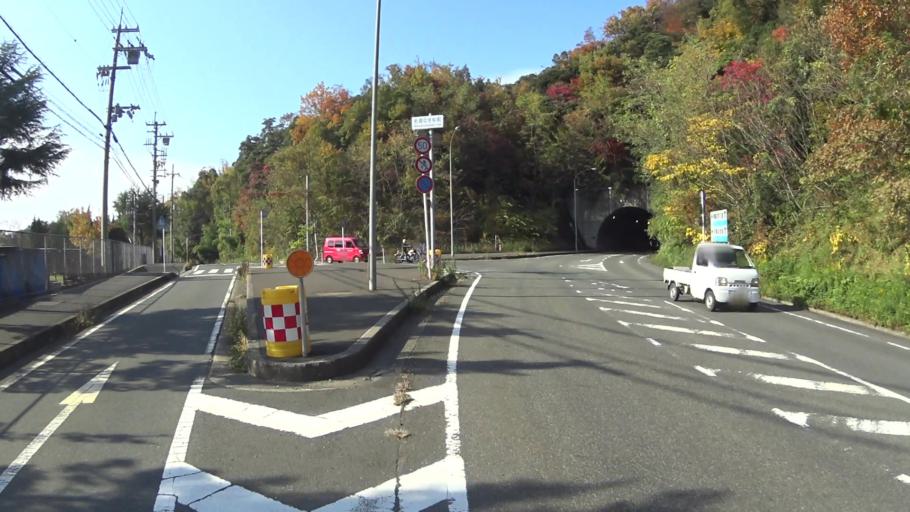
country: JP
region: Kyoto
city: Maizuru
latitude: 35.5059
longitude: 135.3981
